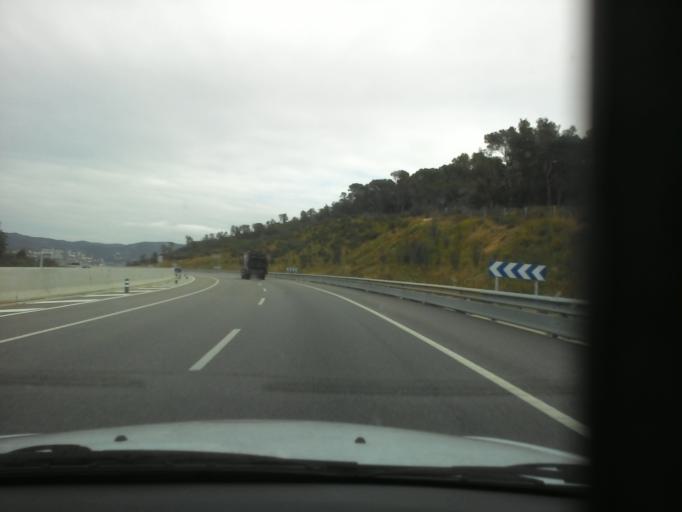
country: ES
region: Catalonia
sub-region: Provincia de Girona
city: Calonge
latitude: 41.8420
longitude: 3.0786
